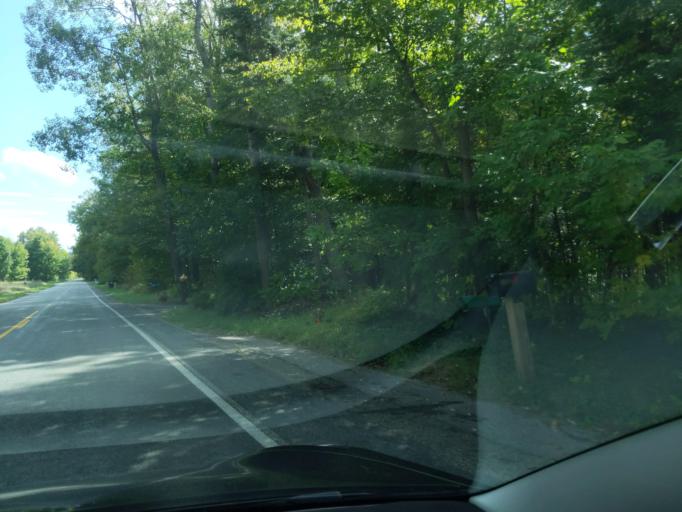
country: US
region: Michigan
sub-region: Antrim County
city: Bellaire
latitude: 44.9958
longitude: -85.2888
